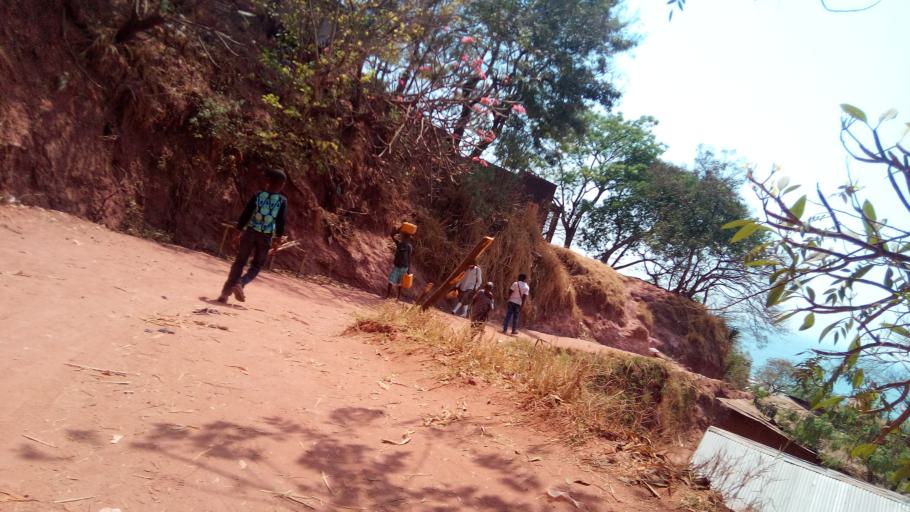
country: CD
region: Katanga
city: Kalemie
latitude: -5.9306
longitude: 29.1905
